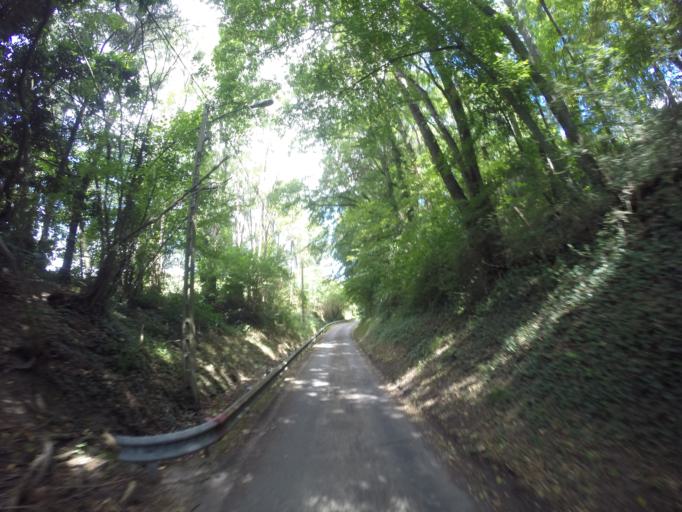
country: FR
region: Centre
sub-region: Departement d'Indre-et-Loire
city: Rochecorbon
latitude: 47.4110
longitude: 0.7167
